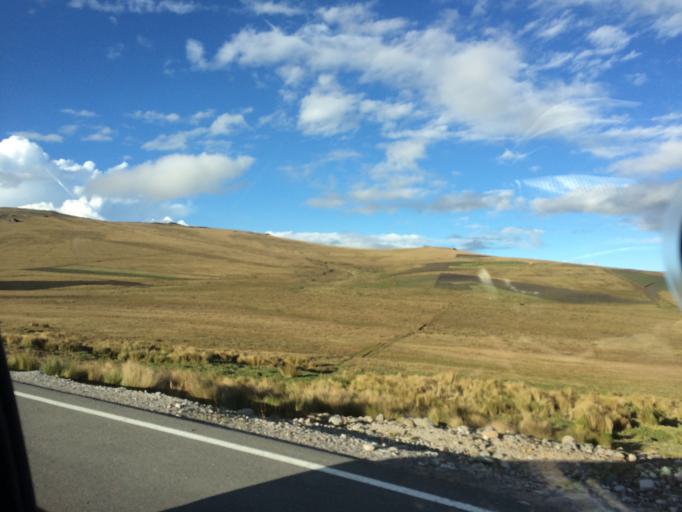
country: EC
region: Chimborazo
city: Alausi
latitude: -2.2304
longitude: -78.6848
